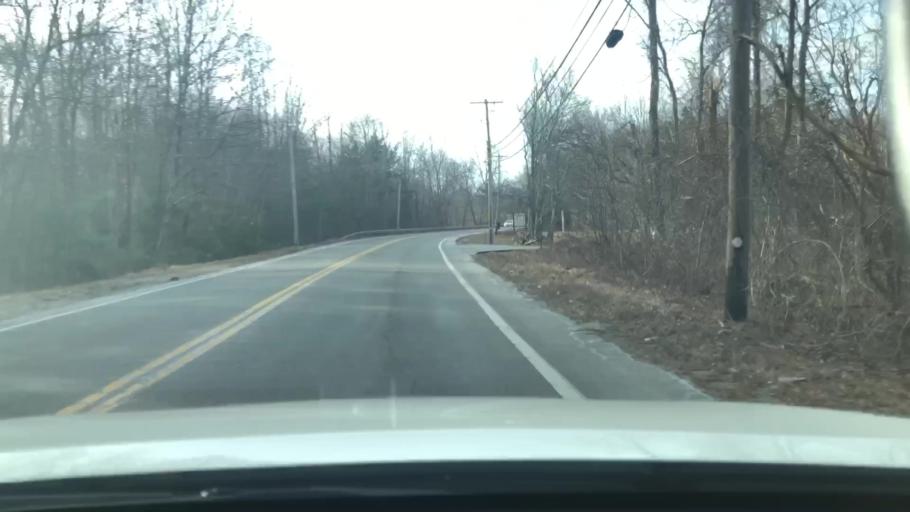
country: US
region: Massachusetts
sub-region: Worcester County
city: Upton
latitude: 42.1552
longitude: -71.5725
